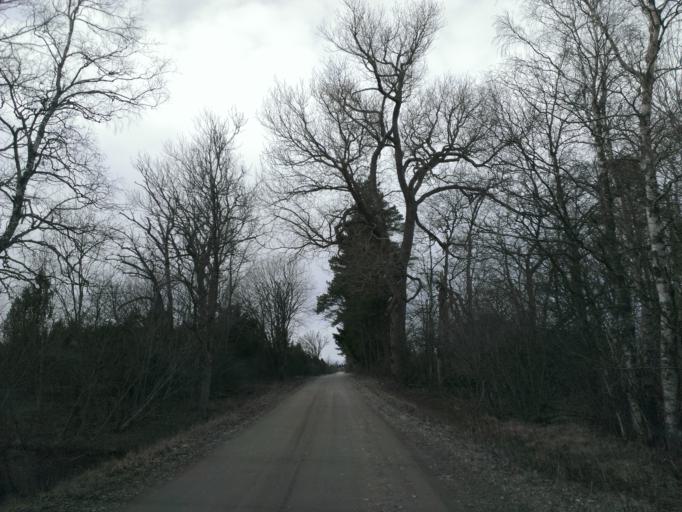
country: EE
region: Laeaene
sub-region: Lihula vald
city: Lihula
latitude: 58.5721
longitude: 23.5483
